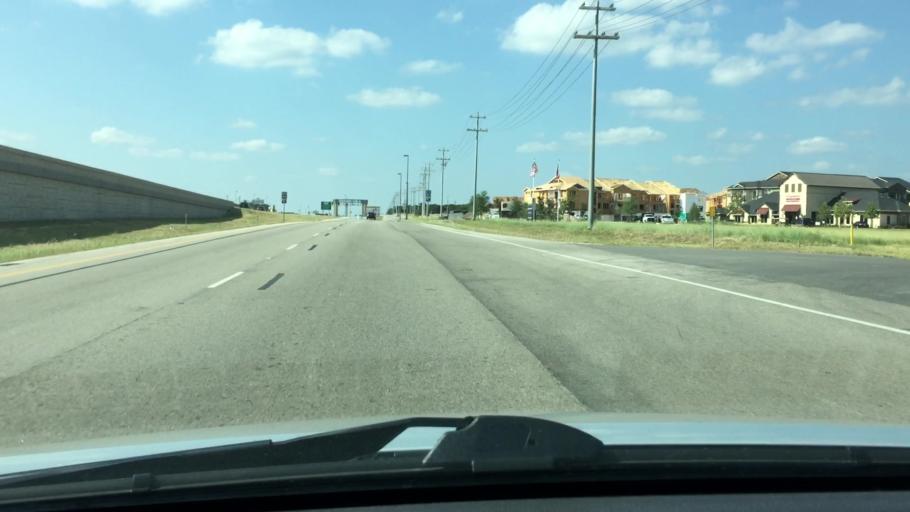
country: US
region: Texas
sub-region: Williamson County
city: Leander
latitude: 30.5652
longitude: -97.8253
